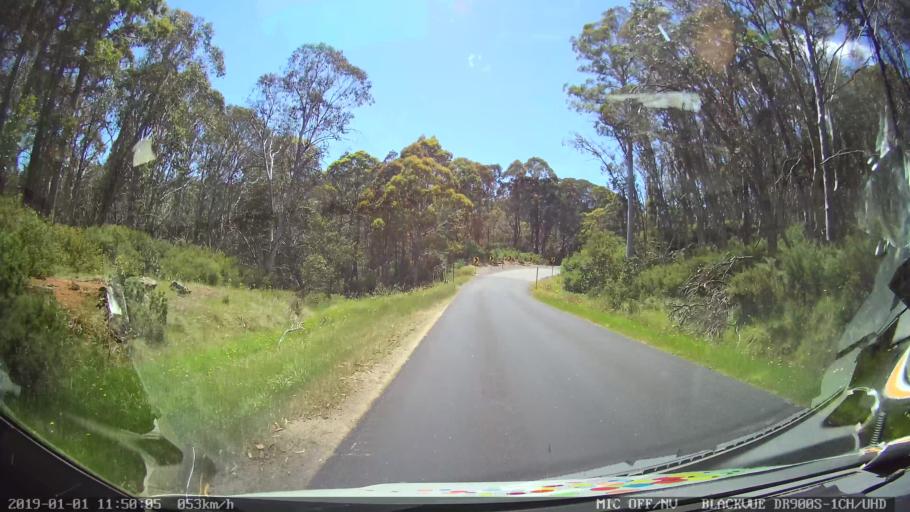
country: AU
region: New South Wales
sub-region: Snowy River
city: Jindabyne
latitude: -35.8909
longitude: 148.4179
